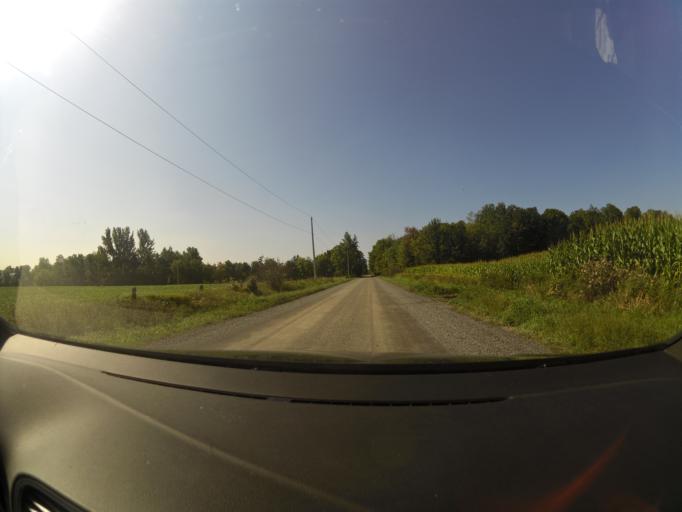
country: CA
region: Ontario
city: Arnprior
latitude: 45.3773
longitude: -76.2716
